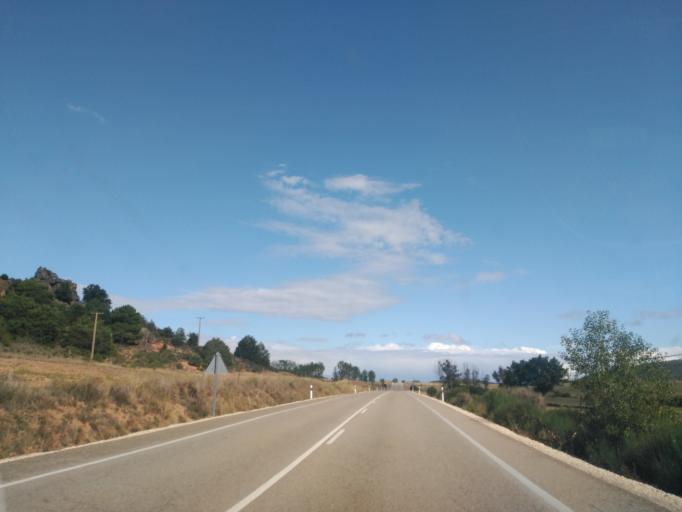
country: ES
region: Castille and Leon
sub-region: Provincia de Burgos
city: Hontoria del Pinar
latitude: 41.8544
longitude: -3.1883
